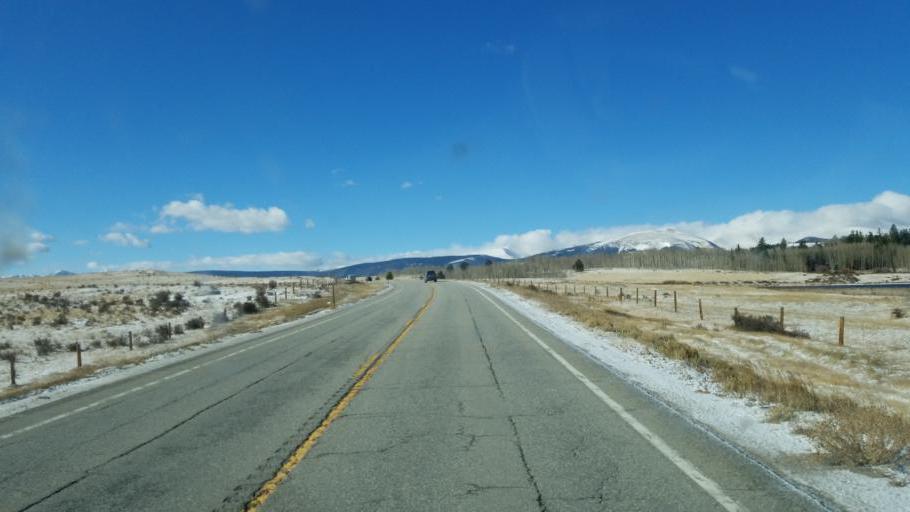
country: US
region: Colorado
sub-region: Park County
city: Fairplay
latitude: 39.2364
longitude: -105.9829
